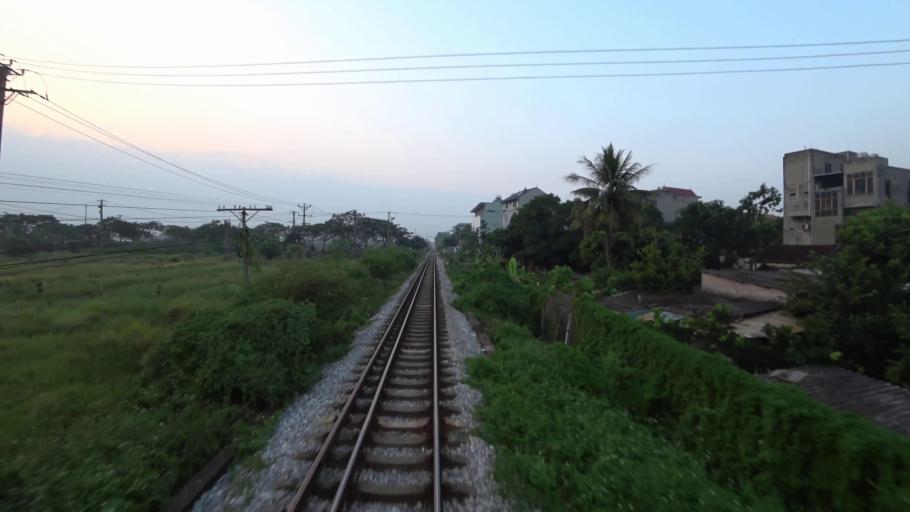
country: VN
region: Ha Noi
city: Dong Anh
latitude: 21.1483
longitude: 105.8580
